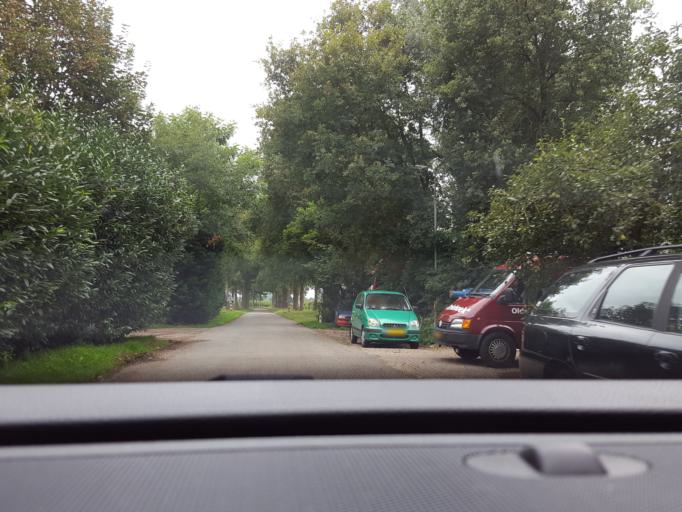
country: NL
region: Gelderland
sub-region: Gemeente Zutphen
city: Leesten
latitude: 52.1163
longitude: 6.2420
